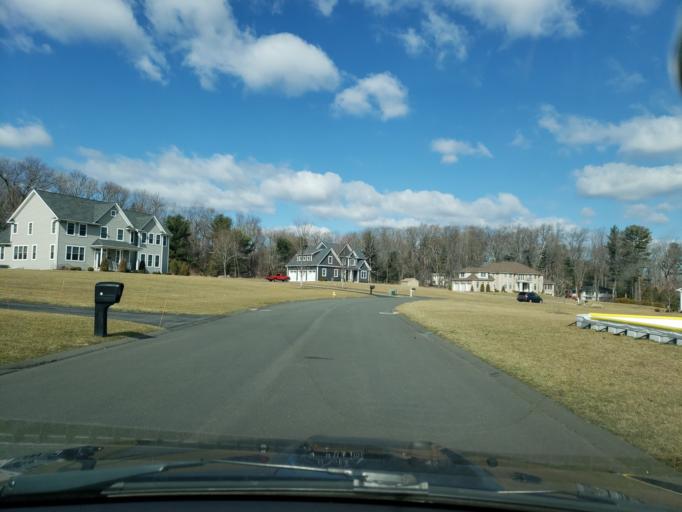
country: US
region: Connecticut
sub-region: Tolland County
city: Somers
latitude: 42.0062
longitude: -72.4819
